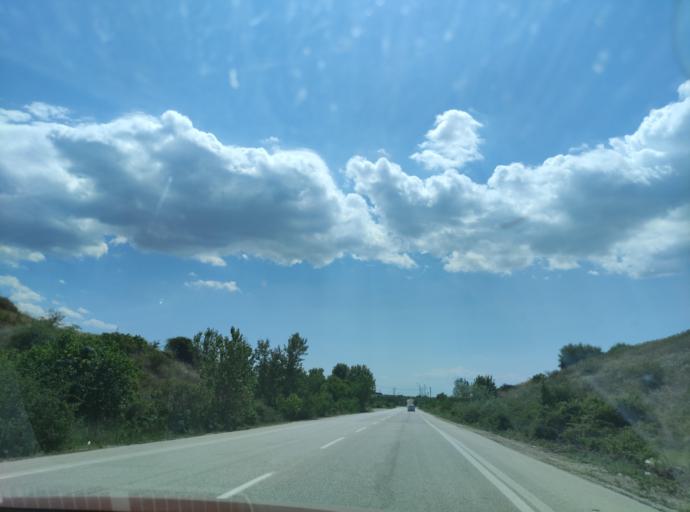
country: GR
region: Central Macedonia
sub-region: Nomos Serron
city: Proti
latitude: 40.9851
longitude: 24.0340
